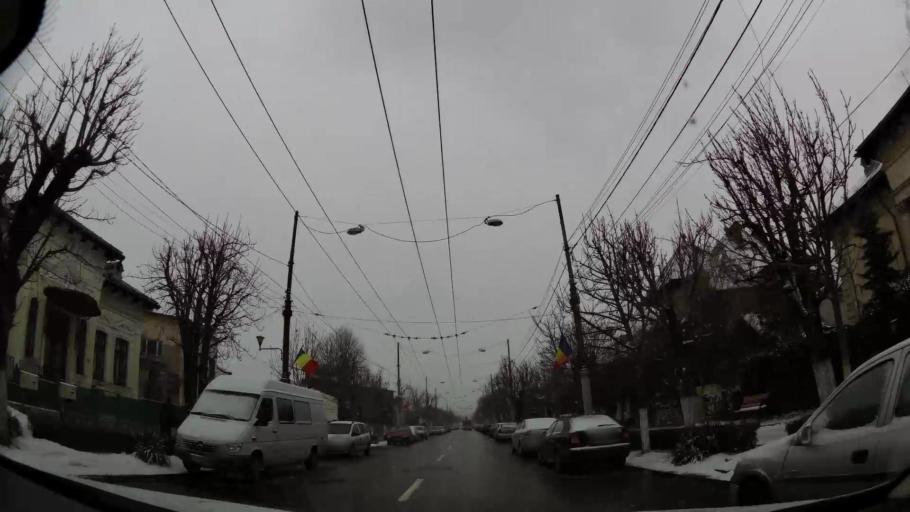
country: RO
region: Dambovita
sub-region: Municipiul Targoviste
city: Targoviste
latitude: 44.9230
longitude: 25.4574
